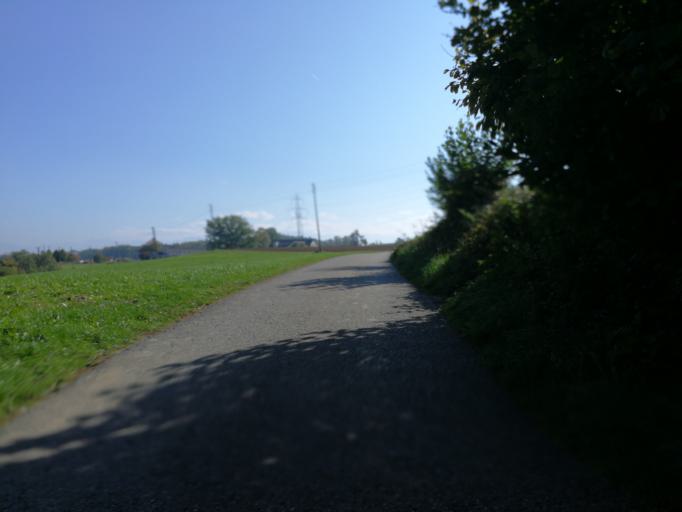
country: CH
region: Zurich
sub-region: Bezirk Uster
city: Hinteregg
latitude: 47.3135
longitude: 8.6860
